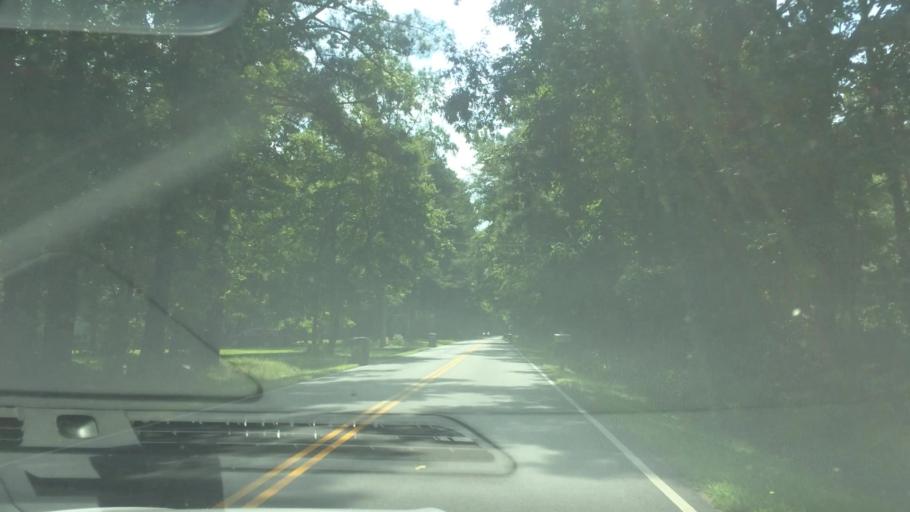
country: US
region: Virginia
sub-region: City of Poquoson
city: Poquoson
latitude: 37.1685
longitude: -76.4345
